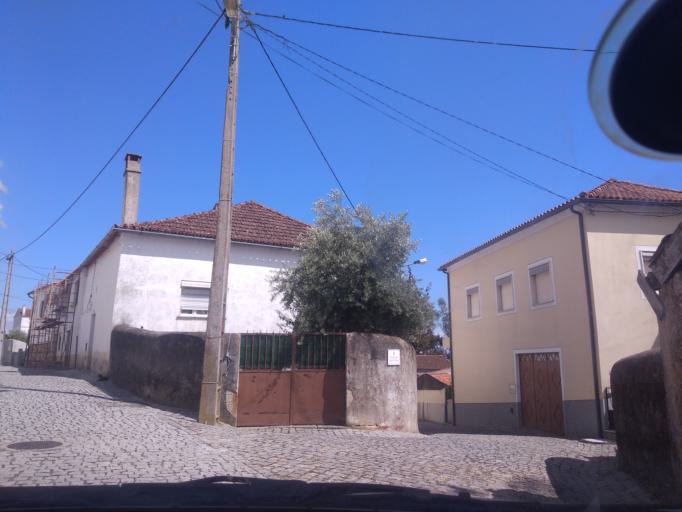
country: PT
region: Castelo Branco
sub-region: Concelho do Fundao
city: Fundao
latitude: 40.2063
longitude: -7.4415
